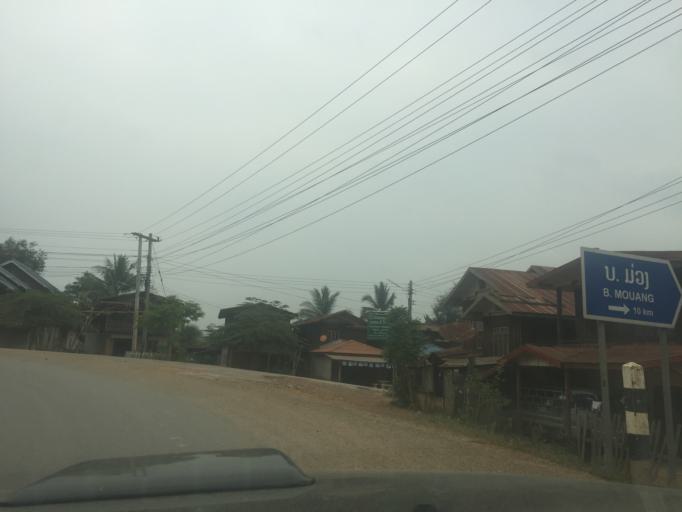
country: LA
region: Vientiane
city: Muang Sanakham
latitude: 18.4034
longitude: 101.5018
